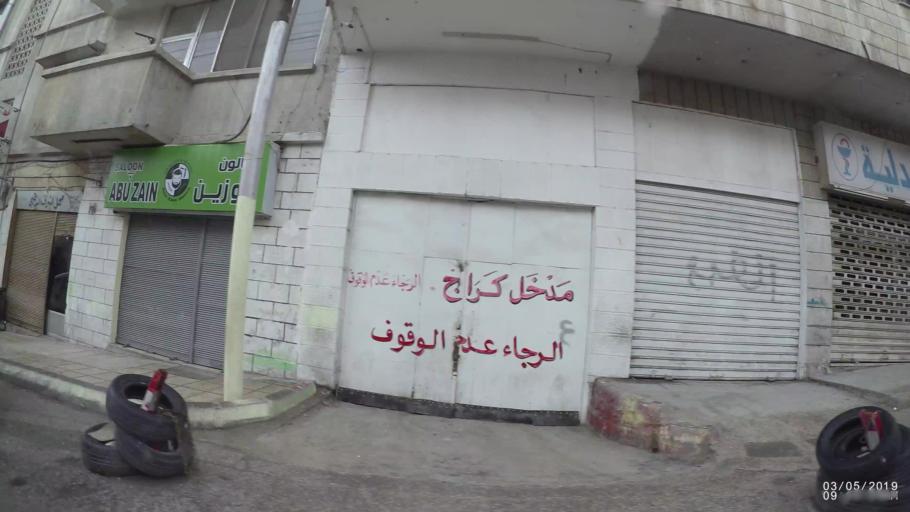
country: JO
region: Amman
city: Amman
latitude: 31.9666
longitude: 35.9287
